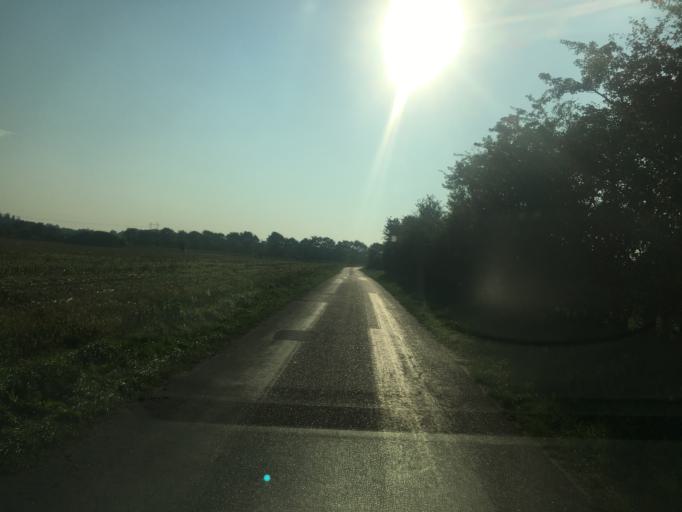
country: DE
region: Schleswig-Holstein
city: Bramstedtlund
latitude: 54.9649
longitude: 9.0647
